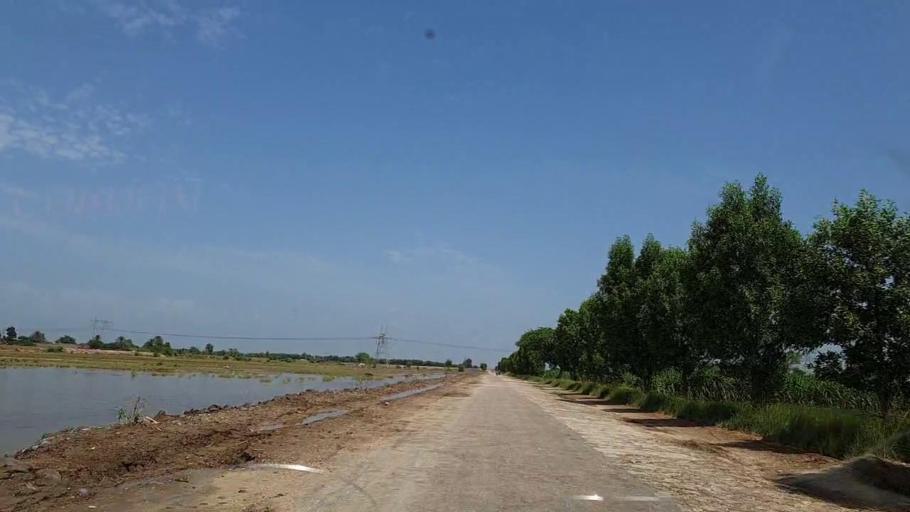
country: PK
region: Sindh
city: Naushahro Firoz
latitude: 26.8281
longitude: 68.1470
